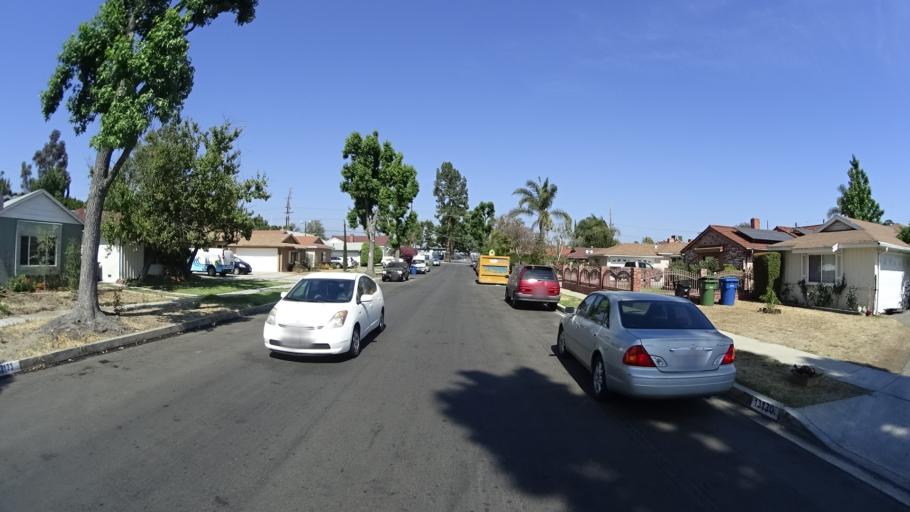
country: US
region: California
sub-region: Los Angeles County
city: Van Nuys
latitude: 34.1958
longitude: -118.4194
